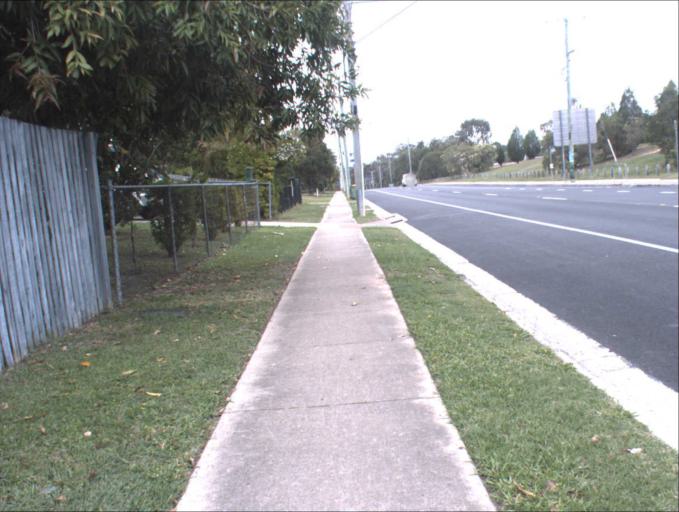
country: AU
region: Queensland
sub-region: Brisbane
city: Sunnybank Hills
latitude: -27.6633
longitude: 153.0529
